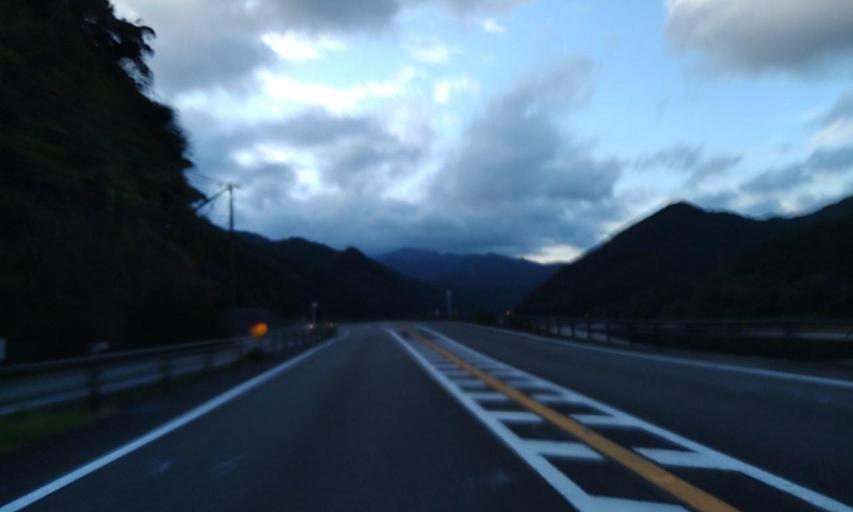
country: JP
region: Wakayama
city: Shingu
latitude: 33.7244
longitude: 135.9610
